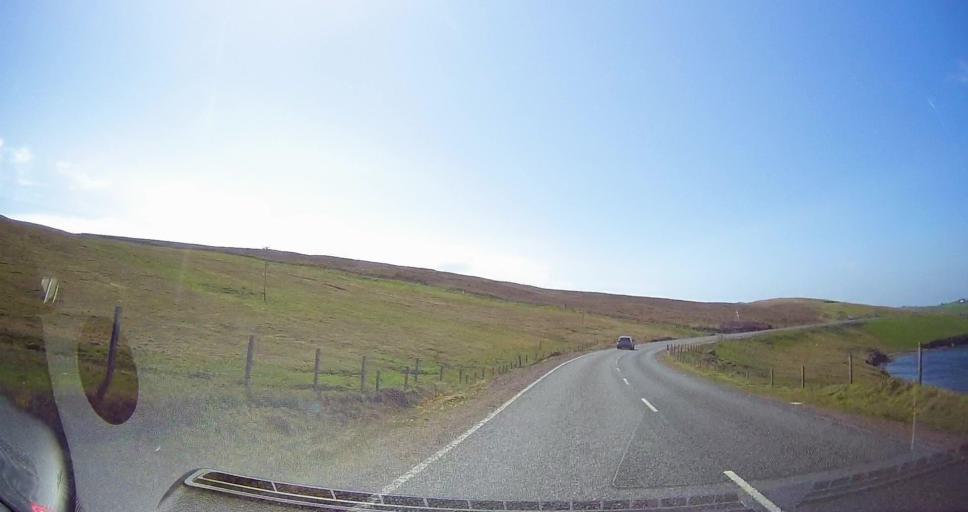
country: GB
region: Scotland
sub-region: Shetland Islands
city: Sandwick
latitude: 60.1100
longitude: -1.2963
